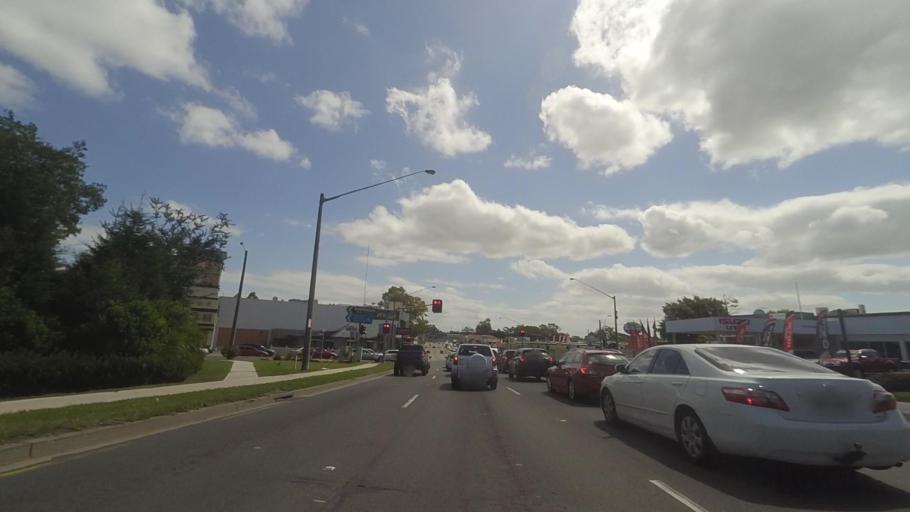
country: AU
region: New South Wales
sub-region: Hornsby Shire
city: Pennant Hills
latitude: -33.7306
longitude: 151.0819
